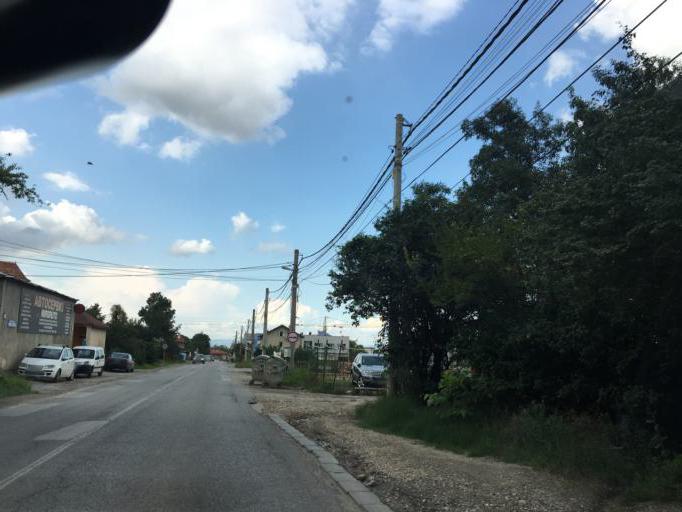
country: BG
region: Sofia-Capital
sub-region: Stolichna Obshtina
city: Sofia
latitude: 42.6366
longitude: 23.3535
